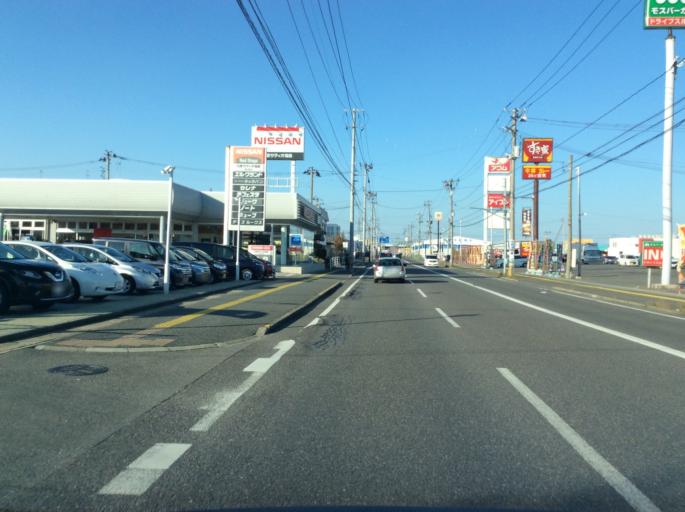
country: JP
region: Fukushima
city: Koriyama
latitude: 37.4066
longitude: 140.3965
